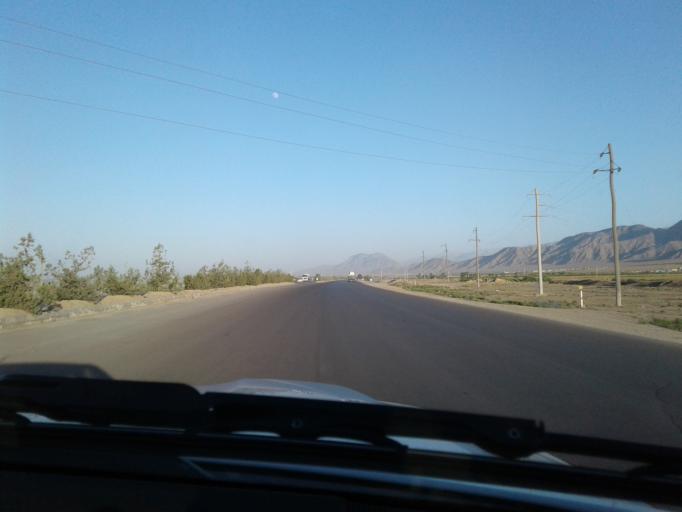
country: TM
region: Ahal
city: Baharly
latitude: 38.2255
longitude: 57.7944
